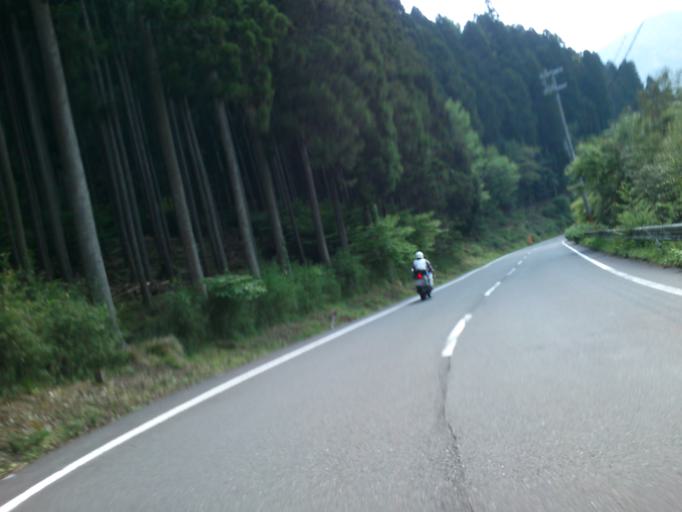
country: JP
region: Kyoto
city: Kameoka
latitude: 35.2575
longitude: 135.5692
